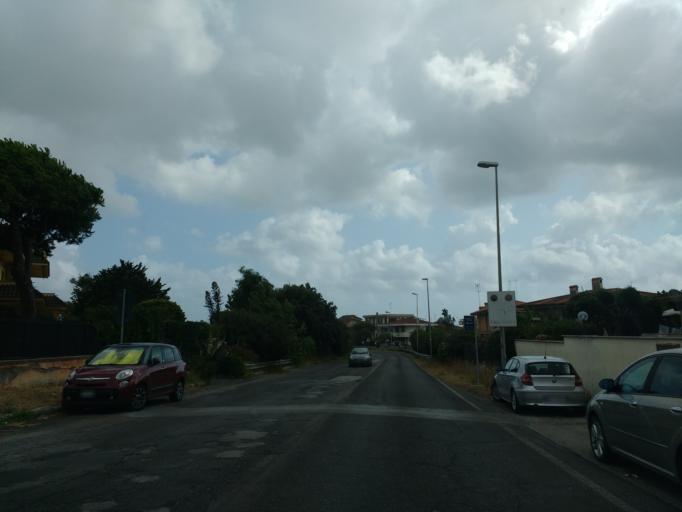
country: IT
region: Latium
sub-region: Citta metropolitana di Roma Capitale
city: Anzio
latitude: 41.4771
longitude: 12.6030
